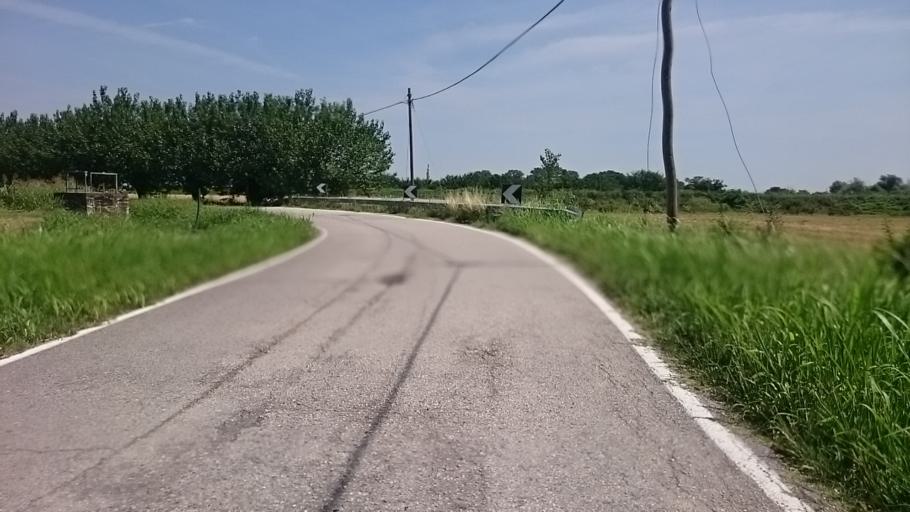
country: IT
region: Veneto
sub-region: Provincia di Vicenza
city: Longare
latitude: 45.4598
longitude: 11.6226
